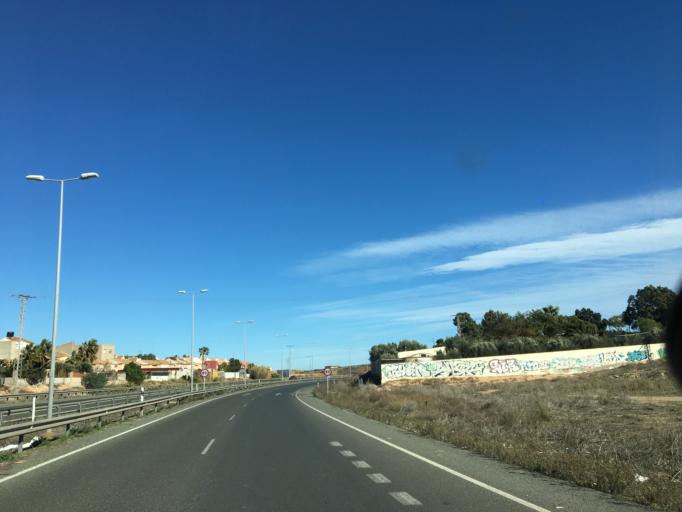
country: ES
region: Murcia
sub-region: Murcia
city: Cartagena
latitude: 37.6323
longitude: -1.0007
